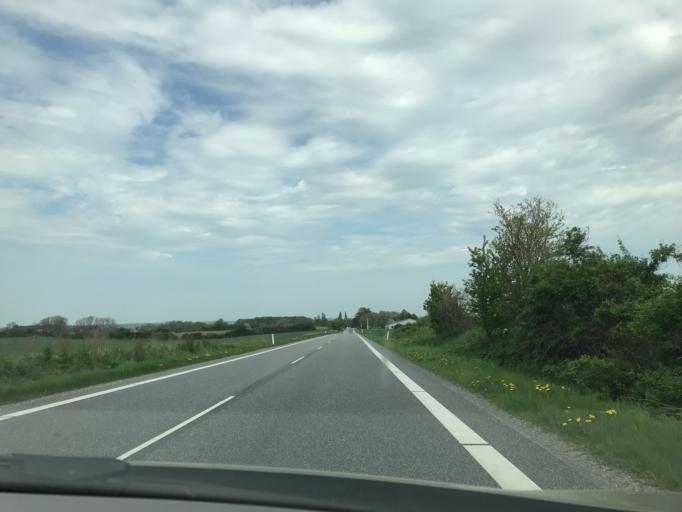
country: DK
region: South Denmark
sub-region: Assens Kommune
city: Assens
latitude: 55.2995
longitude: 9.9412
